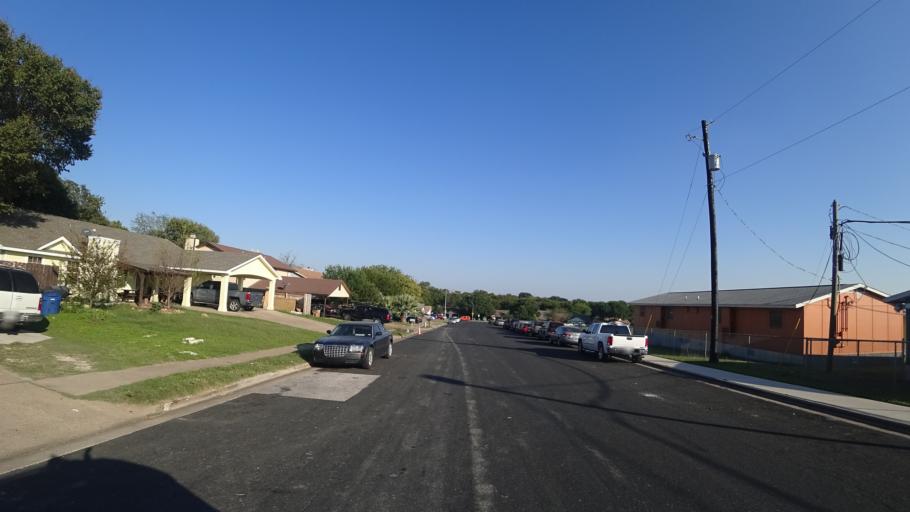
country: US
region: Texas
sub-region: Travis County
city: Wells Branch
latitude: 30.3557
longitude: -97.6787
